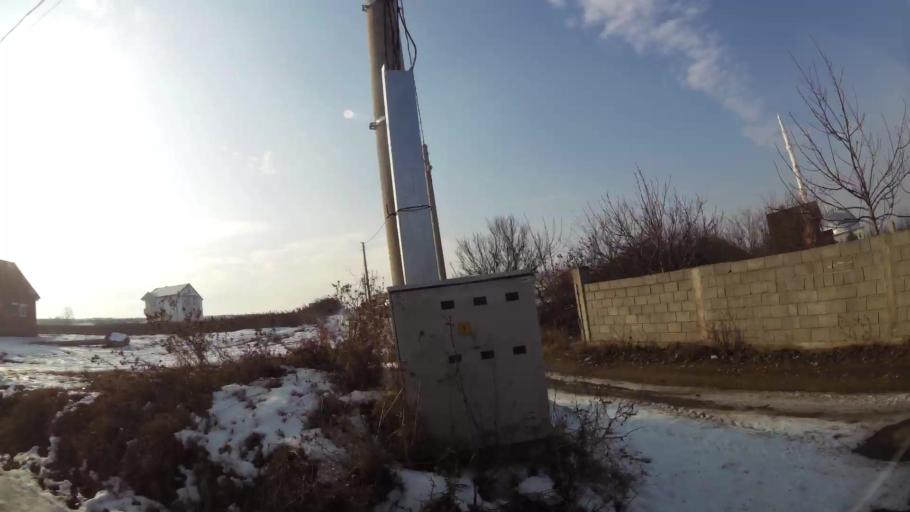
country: MK
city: Creshevo
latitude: 42.0183
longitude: 21.5041
